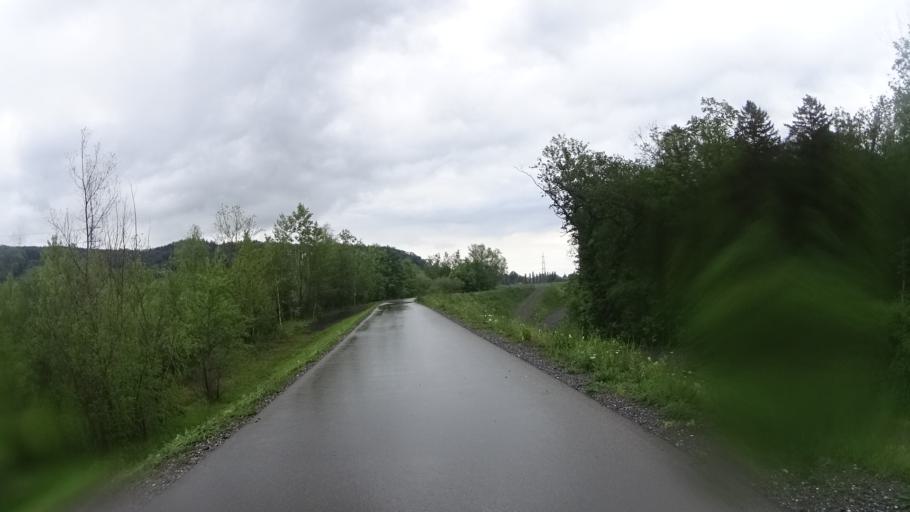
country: AT
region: Vorarlberg
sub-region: Politischer Bezirk Feldkirch
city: Meiningen
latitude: 47.2973
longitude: 9.5591
